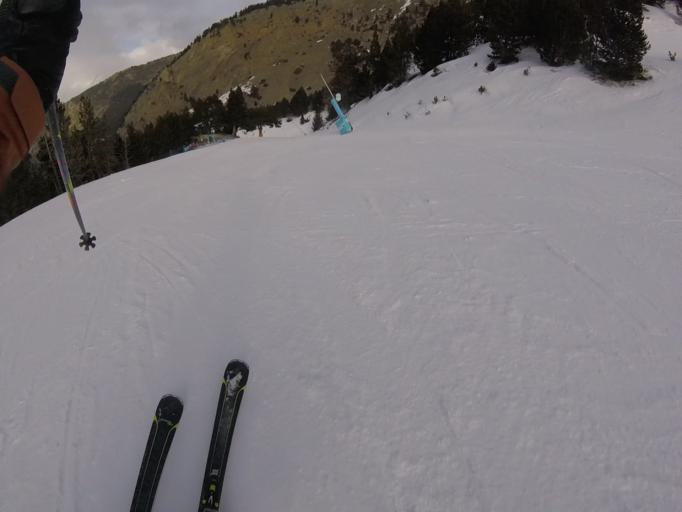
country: AD
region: Canillo
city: Canillo
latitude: 42.5483
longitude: 1.6159
